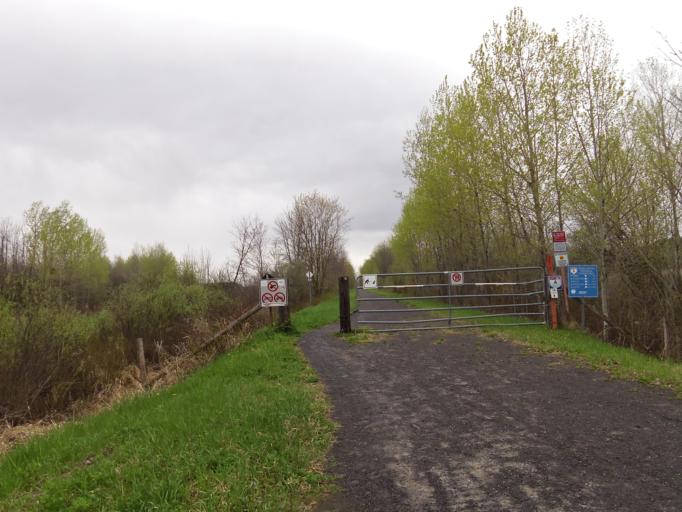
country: CA
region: Ontario
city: Bourget
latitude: 45.4397
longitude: -75.1784
